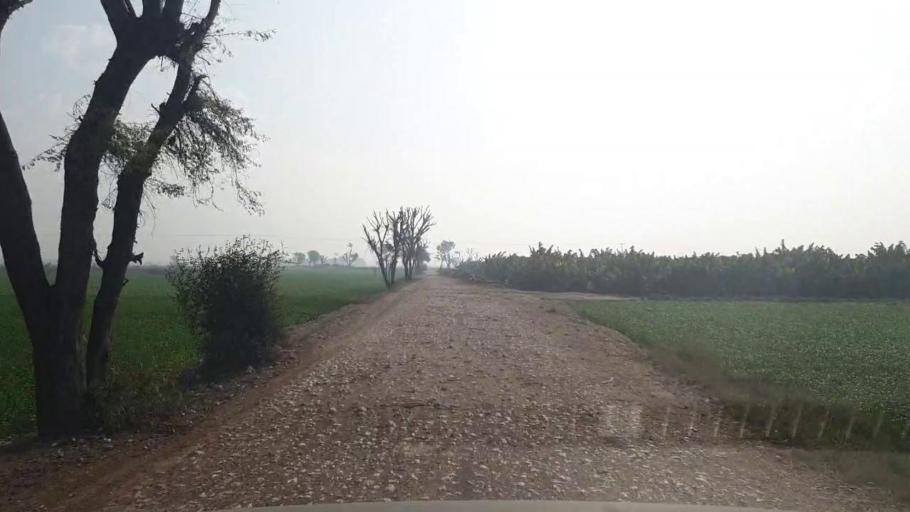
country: PK
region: Sindh
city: Hala
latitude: 25.8595
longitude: 68.4316
